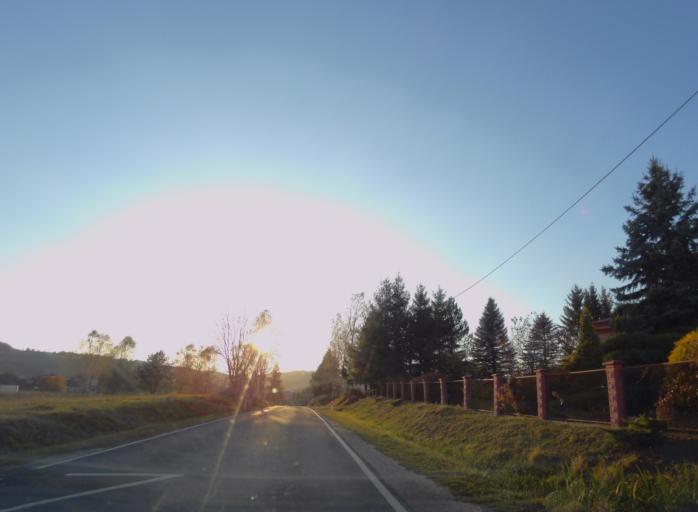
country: PL
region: Subcarpathian Voivodeship
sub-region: Powiat leski
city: Polanczyk
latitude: 49.3824
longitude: 22.4261
